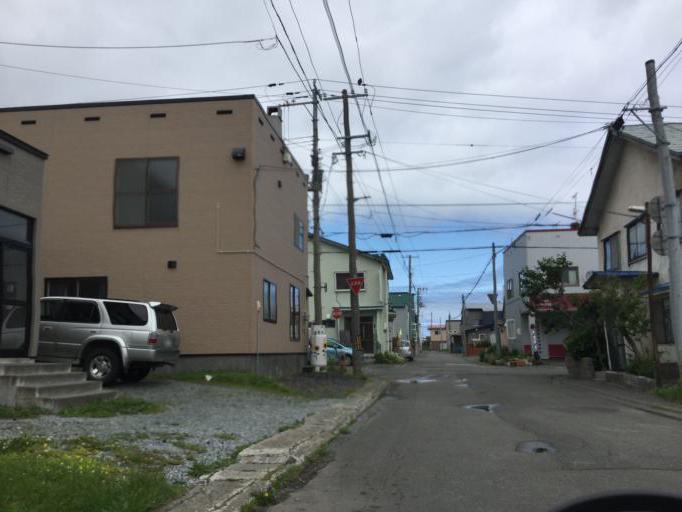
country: JP
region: Hokkaido
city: Wakkanai
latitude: 45.4216
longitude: 141.6733
